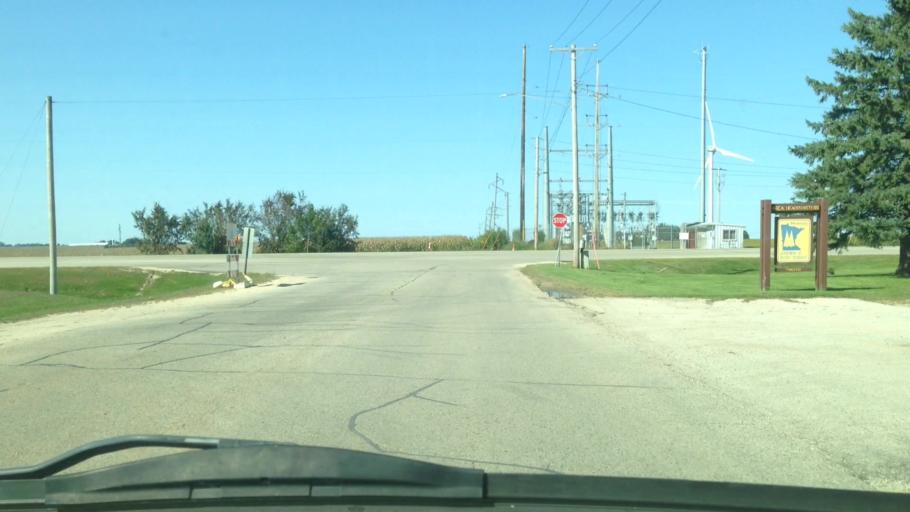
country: US
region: Minnesota
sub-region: Winona County
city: Lewiston
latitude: 43.9873
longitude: -91.8692
